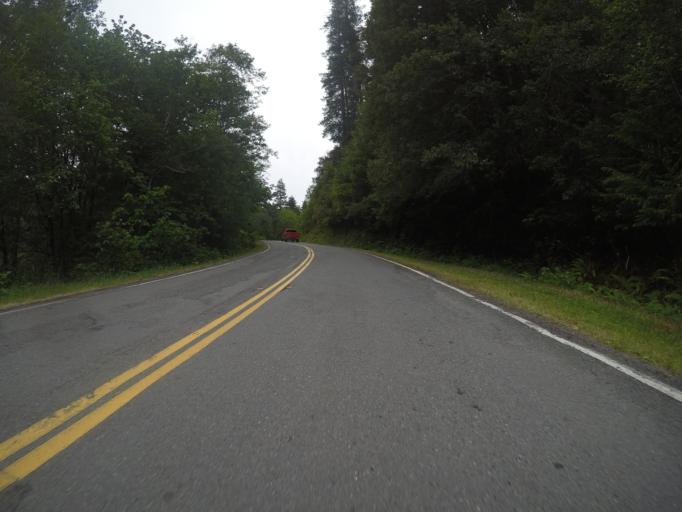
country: US
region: California
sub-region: Del Norte County
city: Bertsch-Oceanview
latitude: 41.7258
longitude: -123.9570
